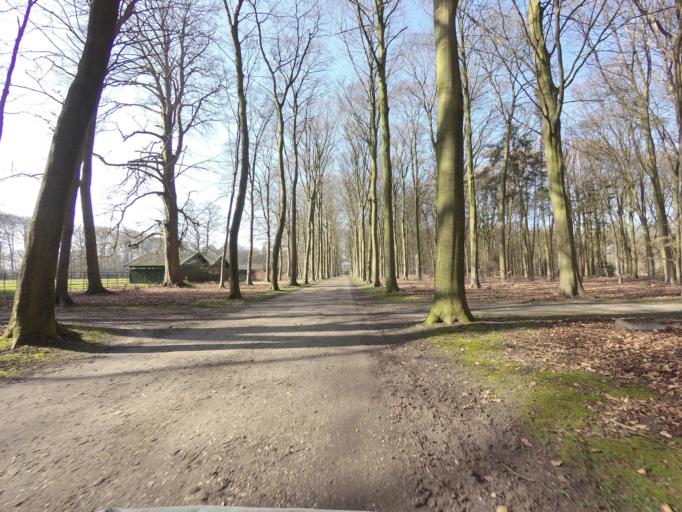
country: NL
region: North Holland
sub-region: Gemeente Wijdemeren
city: Kortenhoef
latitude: 52.2303
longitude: 5.1351
